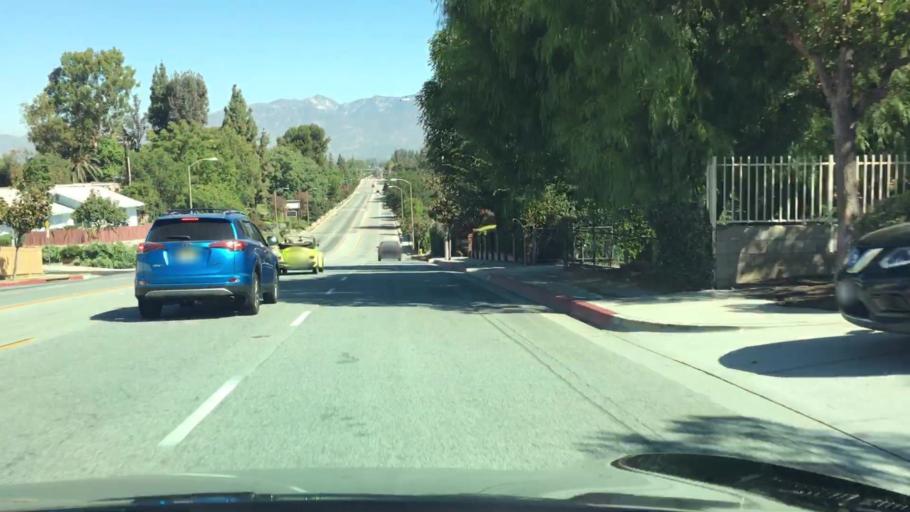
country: US
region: California
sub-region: Los Angeles County
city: South San Gabriel
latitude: 34.0436
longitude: -118.0818
